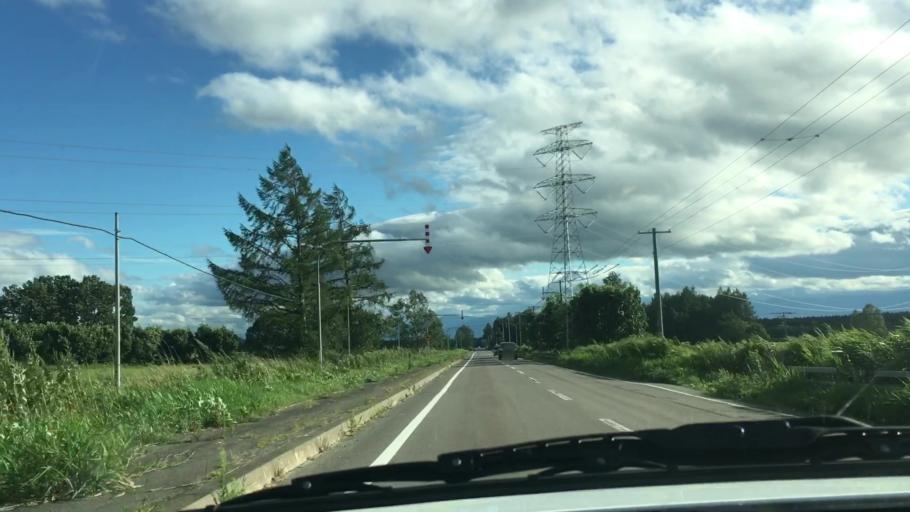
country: JP
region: Hokkaido
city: Otofuke
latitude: 43.1761
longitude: 143.0071
